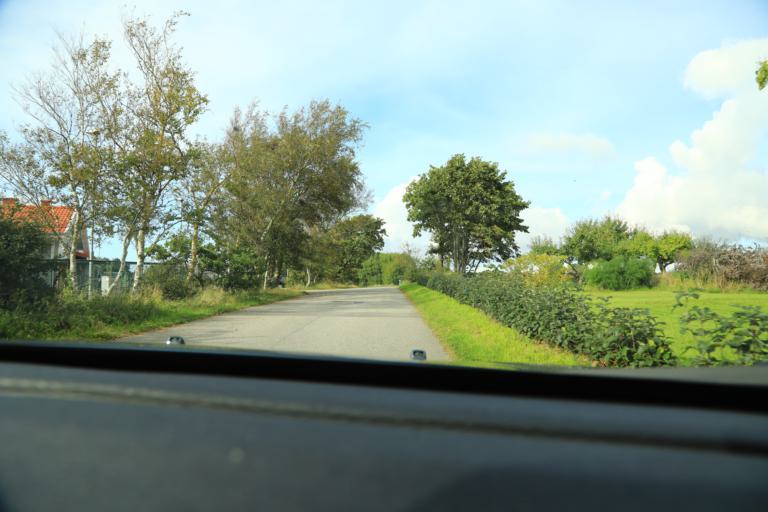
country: SE
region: Halland
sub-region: Varbergs Kommun
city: Traslovslage
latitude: 57.0433
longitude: 12.3165
